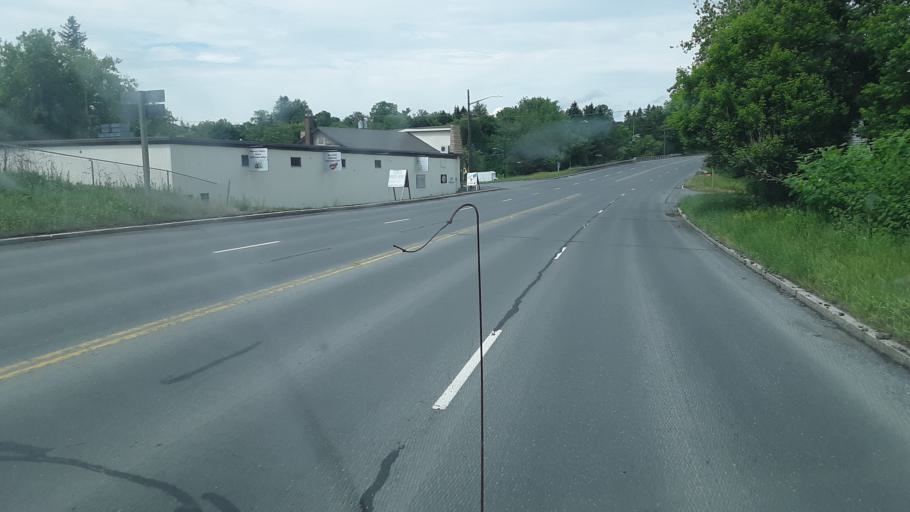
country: US
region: Maine
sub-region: Aroostook County
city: Caribou
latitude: 46.8559
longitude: -68.0060
